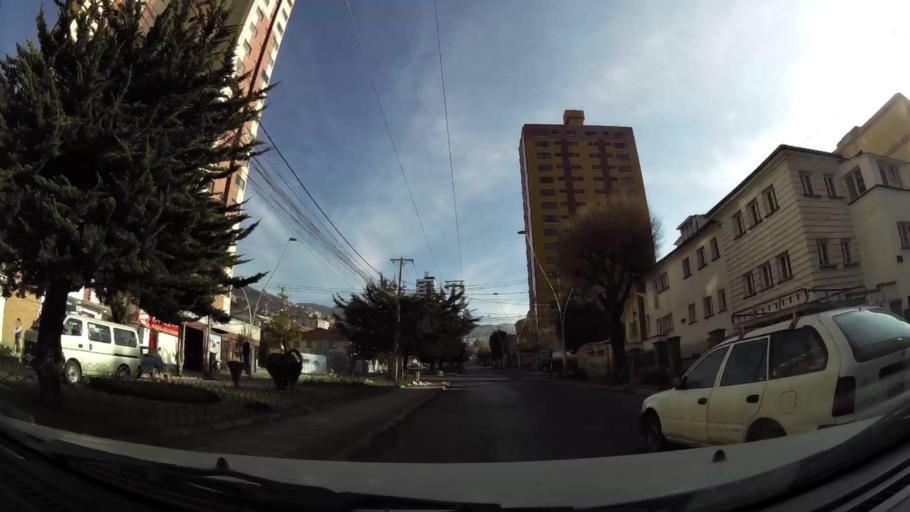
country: BO
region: La Paz
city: La Paz
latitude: -16.4895
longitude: -68.1215
